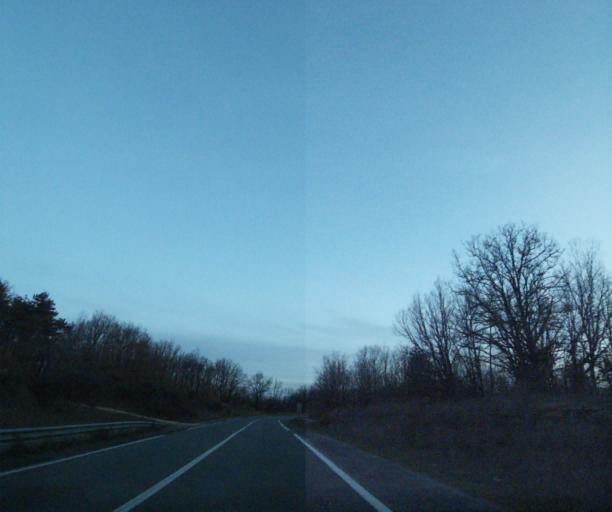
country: FR
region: Midi-Pyrenees
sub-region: Departement du Lot
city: Pradines
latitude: 44.5304
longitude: 1.4666
